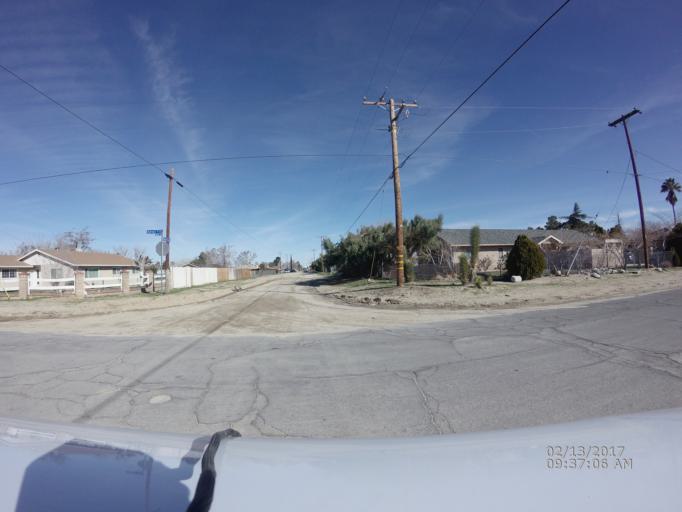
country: US
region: California
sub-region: Los Angeles County
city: Littlerock
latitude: 34.5393
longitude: -117.9669
